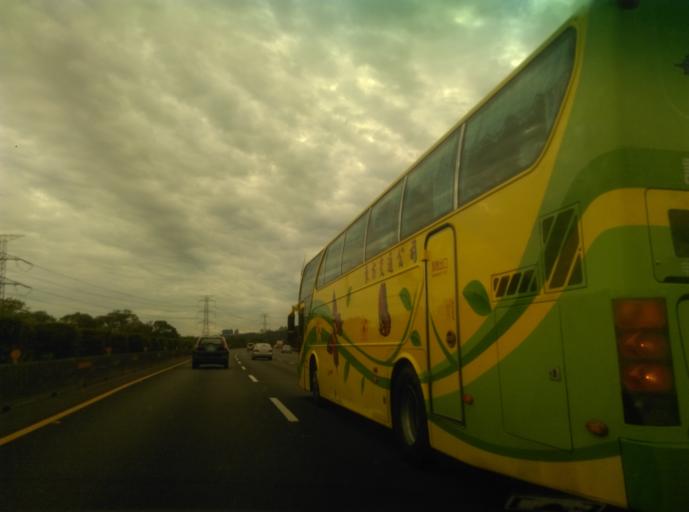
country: TW
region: Taiwan
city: Daxi
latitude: 24.9284
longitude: 121.3105
